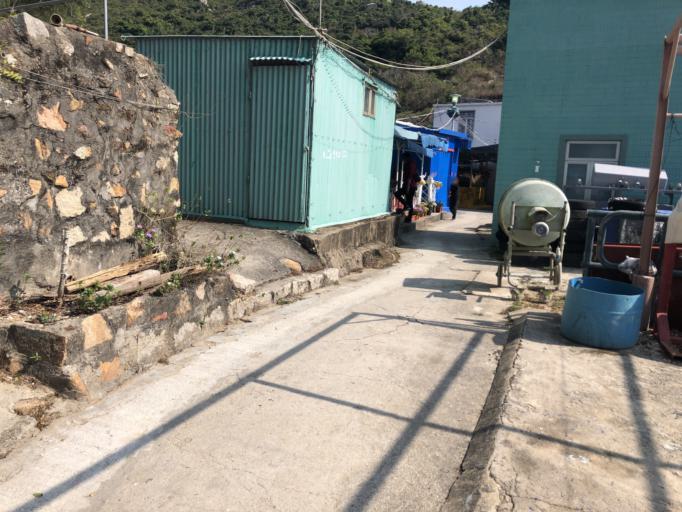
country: HK
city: Sok Kwu Wan
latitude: 22.1652
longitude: 114.2541
